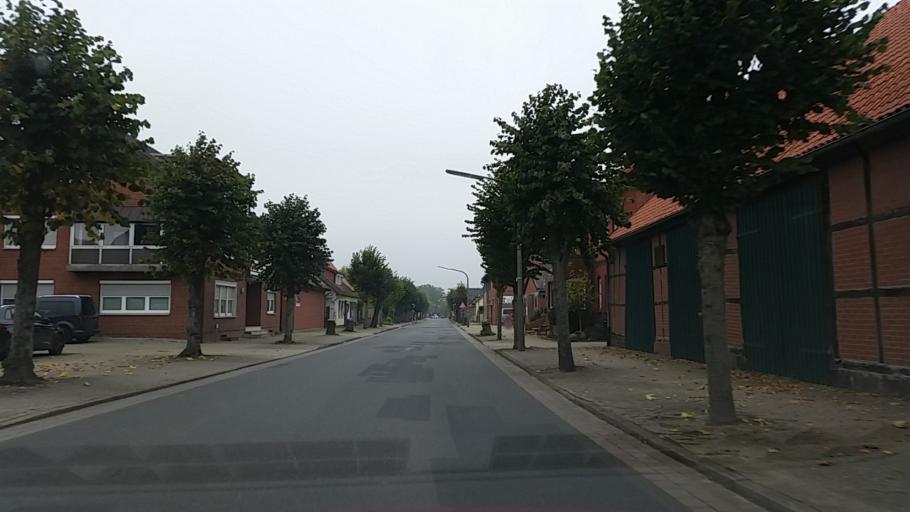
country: DE
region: Lower Saxony
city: Wittingen
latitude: 52.6761
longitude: 10.7039
